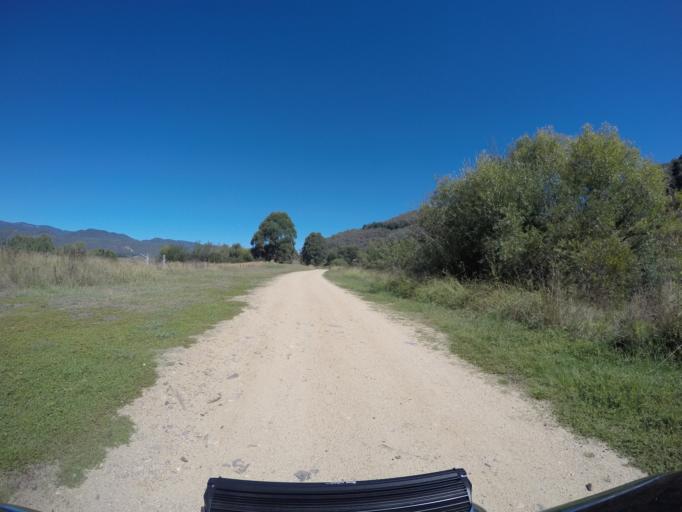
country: AU
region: New South Wales
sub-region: Snowy River
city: Jindabyne
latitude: -36.2171
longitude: 148.1077
